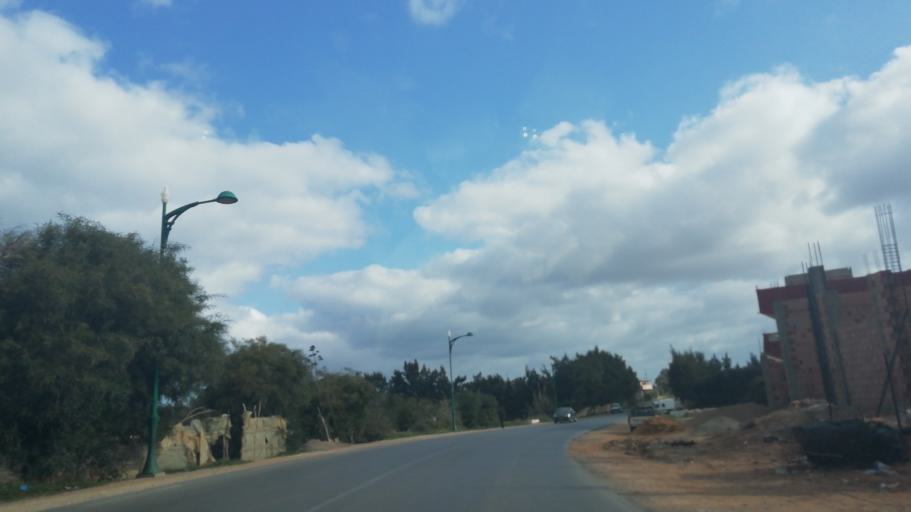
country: DZ
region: Relizane
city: Mazouna
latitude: 36.2790
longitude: 0.6378
